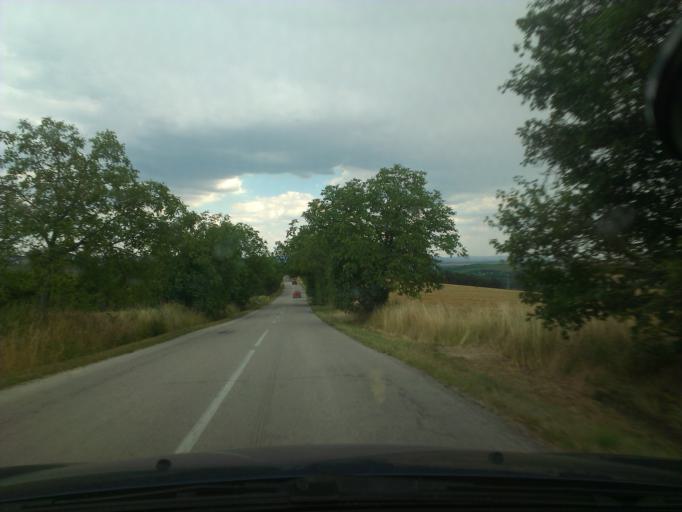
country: SK
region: Trnavsky
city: Vrbove
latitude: 48.6570
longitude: 17.6987
